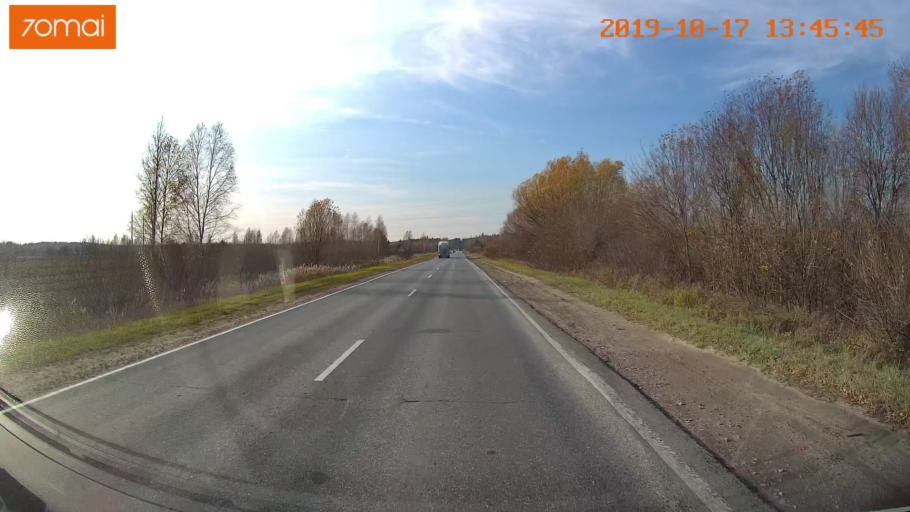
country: RU
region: Rjazan
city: Tuma
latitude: 55.1471
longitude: 40.5072
